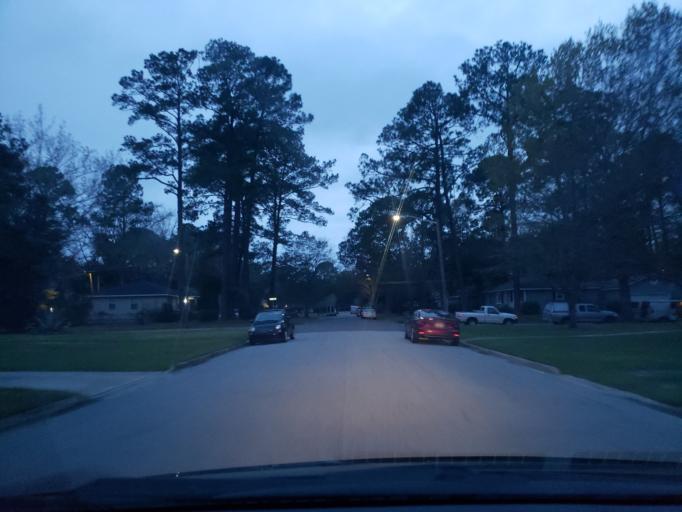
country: US
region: Georgia
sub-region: Chatham County
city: Thunderbolt
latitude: 32.0301
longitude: -81.1024
